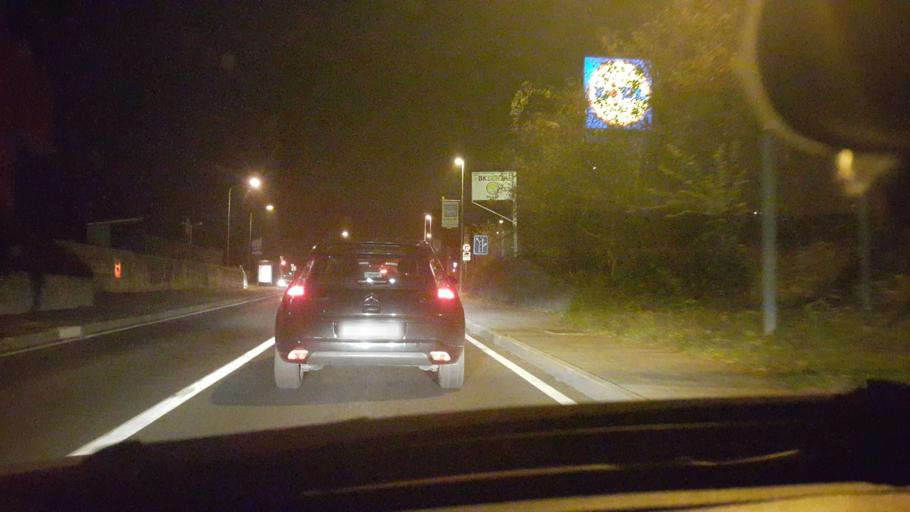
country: SI
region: Maribor
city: Kamnica
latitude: 46.5660
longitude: 15.6228
